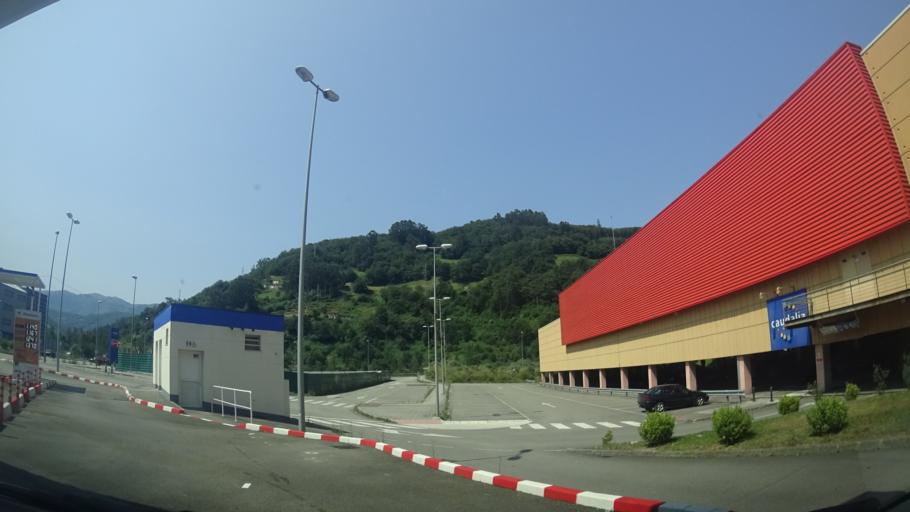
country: ES
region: Asturias
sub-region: Province of Asturias
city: Mieres
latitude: 43.2279
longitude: -5.7812
